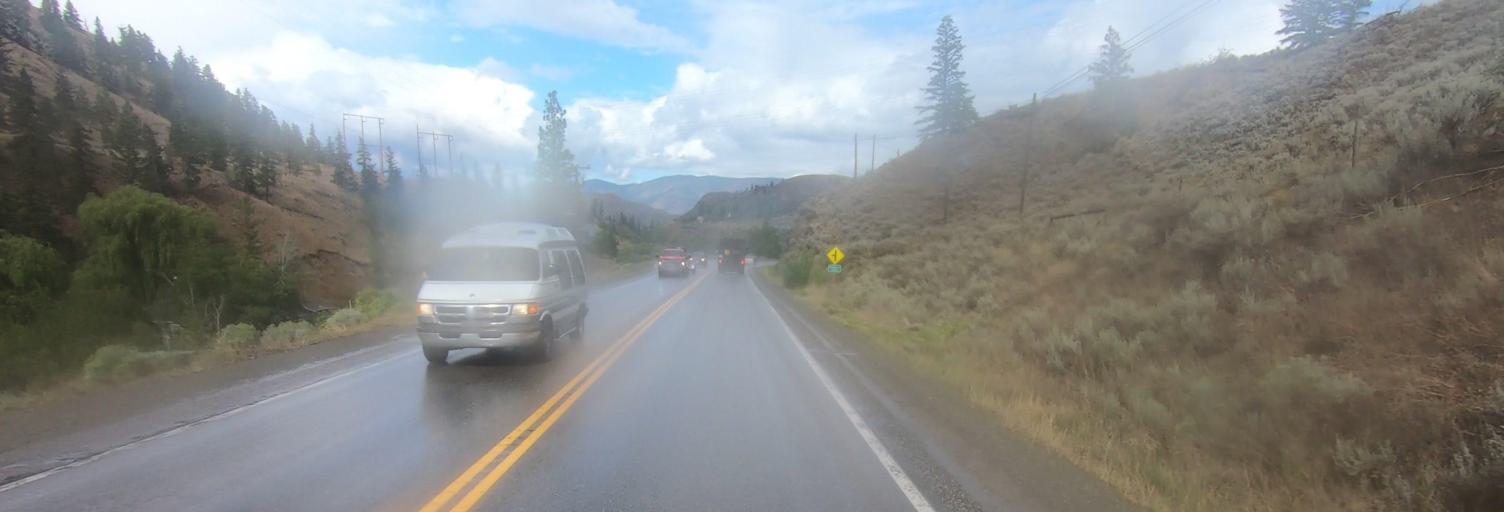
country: CA
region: British Columbia
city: Kamloops
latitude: 50.6760
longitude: -120.5750
